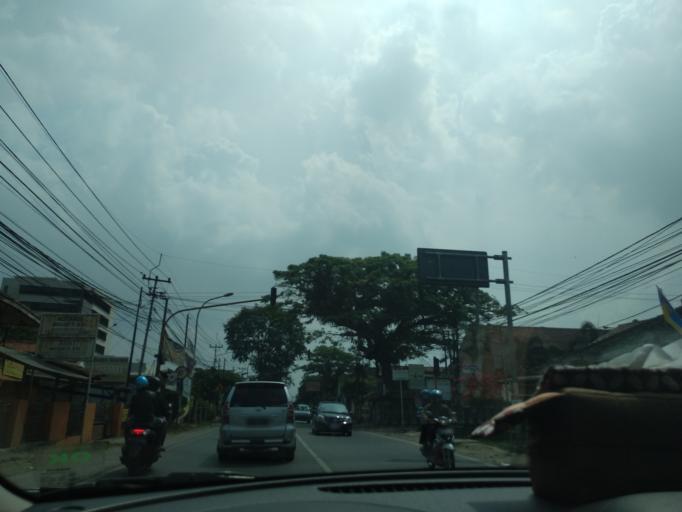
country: ID
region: West Java
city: Padalarang
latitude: -6.8623
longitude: 107.5019
